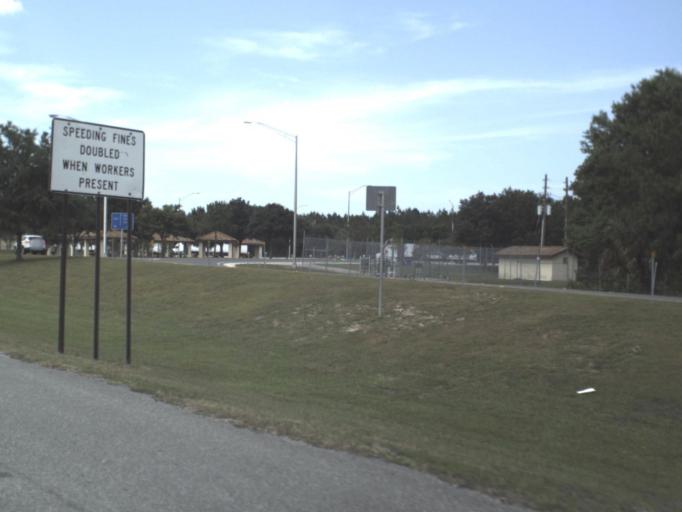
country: US
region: Florida
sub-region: Saint Johns County
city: Palm Valley
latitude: 30.0893
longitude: -81.4975
